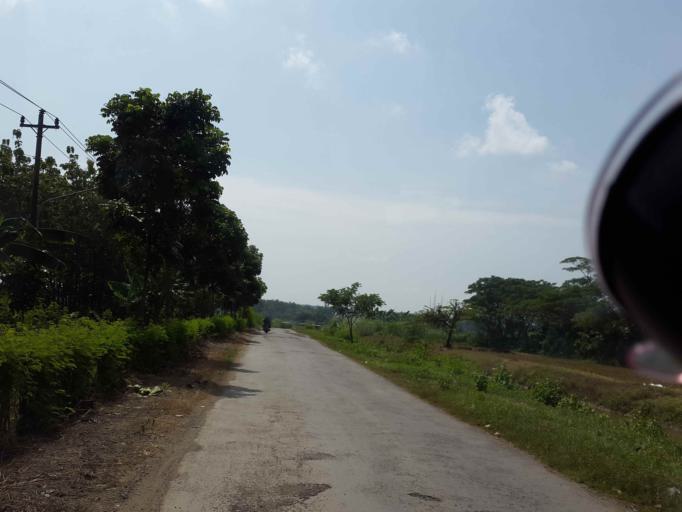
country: ID
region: Central Java
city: Pemalang
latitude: -6.9502
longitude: 109.3556
